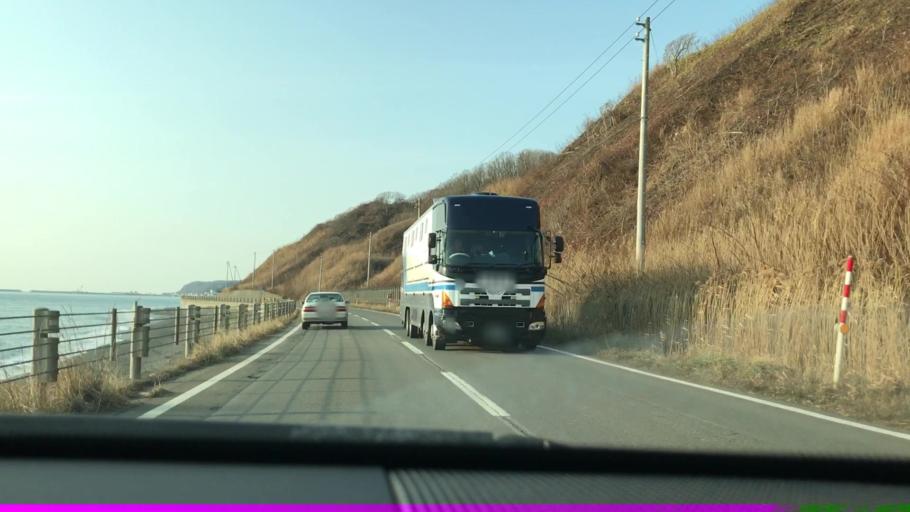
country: JP
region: Hokkaido
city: Shizunai-furukawacho
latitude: 42.2360
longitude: 142.5985
